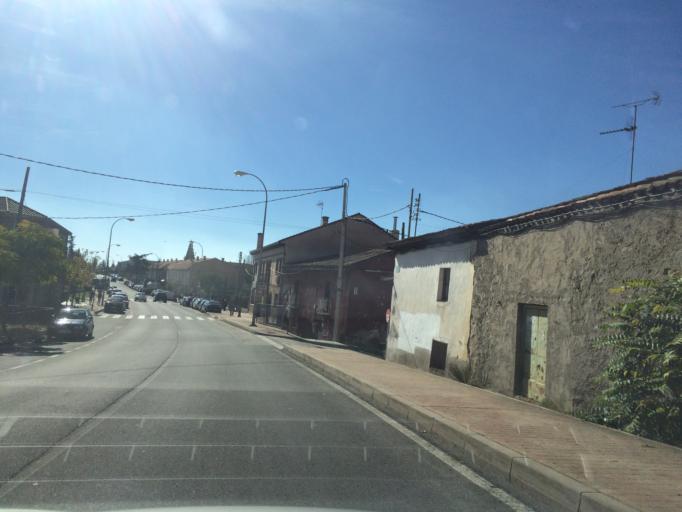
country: ES
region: Madrid
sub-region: Provincia de Madrid
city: La Cabrera
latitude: 40.8654
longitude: -3.6127
